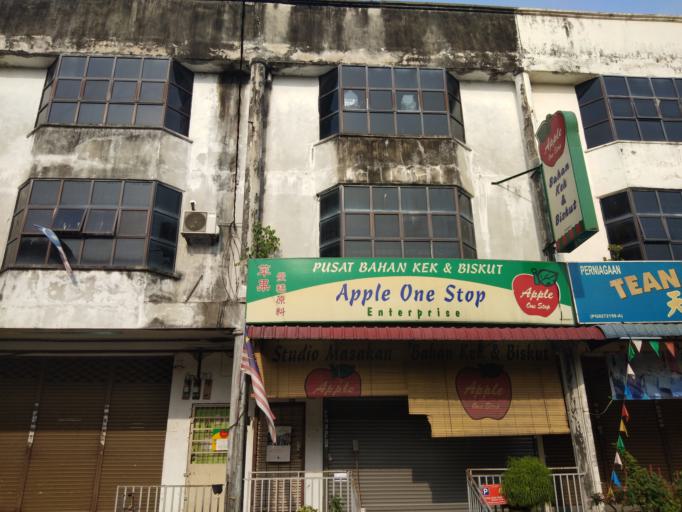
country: MY
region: Kedah
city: Kulim
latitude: 5.3778
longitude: 100.5397
